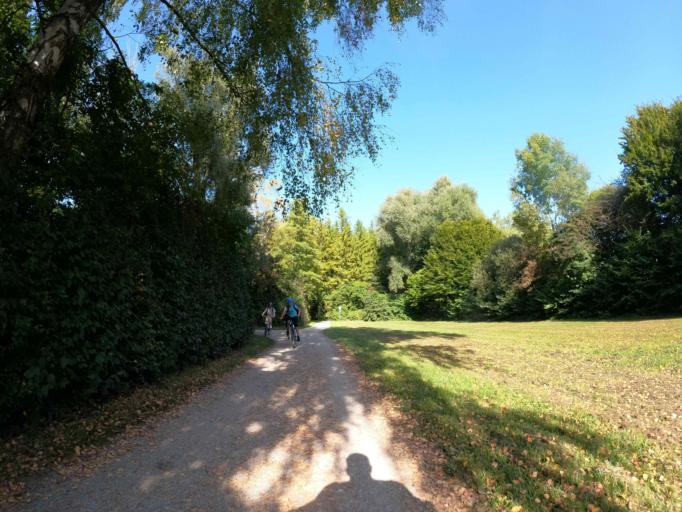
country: DE
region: Bavaria
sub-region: Upper Bavaria
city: Karlsfeld
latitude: 48.2254
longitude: 11.4405
